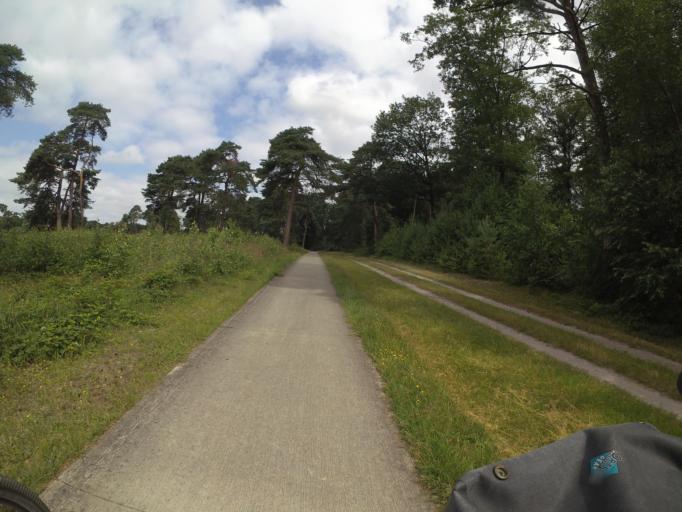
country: NL
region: Gelderland
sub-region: Gemeente Epe
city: Epe
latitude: 52.3918
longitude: 5.9733
